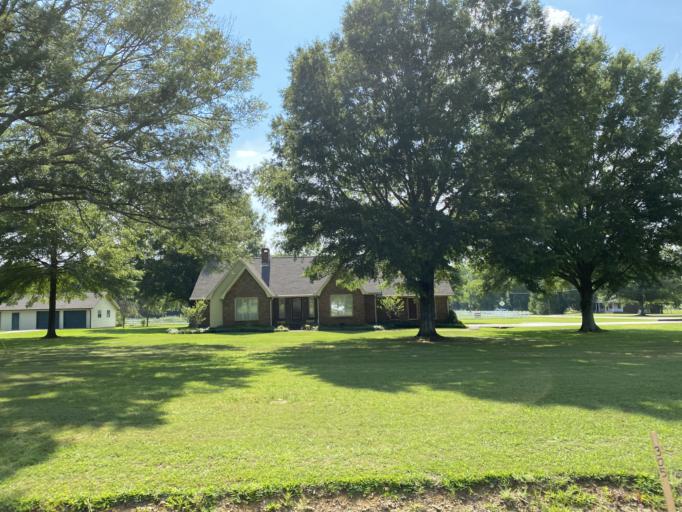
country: US
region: Alabama
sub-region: Lawrence County
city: Town Creek
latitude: 34.6590
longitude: -87.4056
